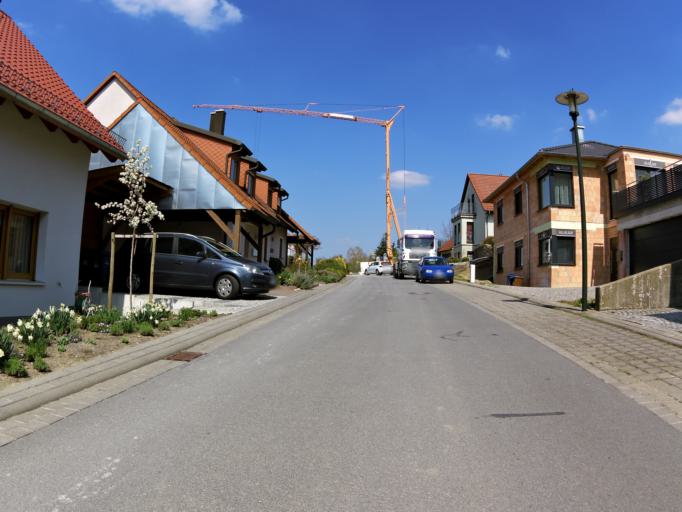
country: DE
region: Bavaria
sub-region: Regierungsbezirk Unterfranken
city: Theilheim
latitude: 49.7572
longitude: 10.0372
